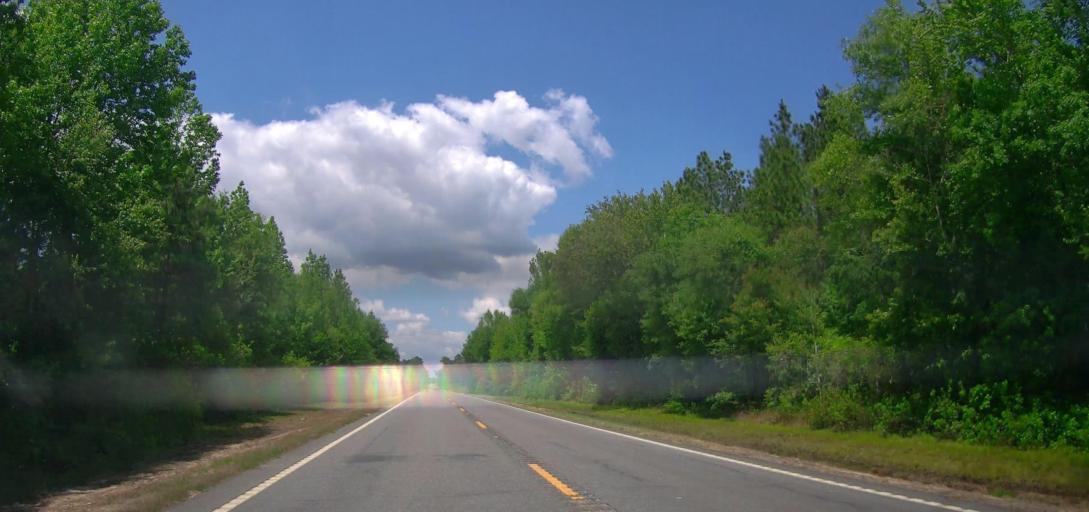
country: US
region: Georgia
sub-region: Treutlen County
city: Soperton
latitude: 32.3910
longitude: -82.5998
